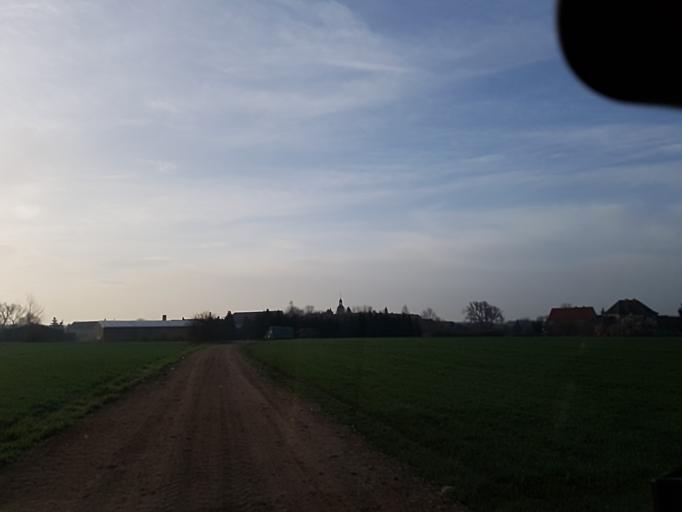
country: DE
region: Brandenburg
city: Falkenberg
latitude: 51.5044
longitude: 13.2815
